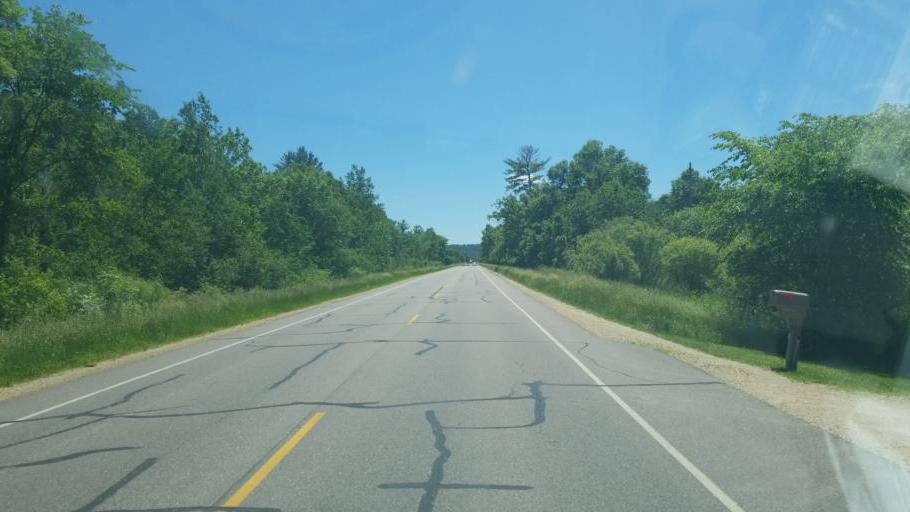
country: US
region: Wisconsin
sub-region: Juneau County
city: Elroy
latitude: 43.6969
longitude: -90.2665
